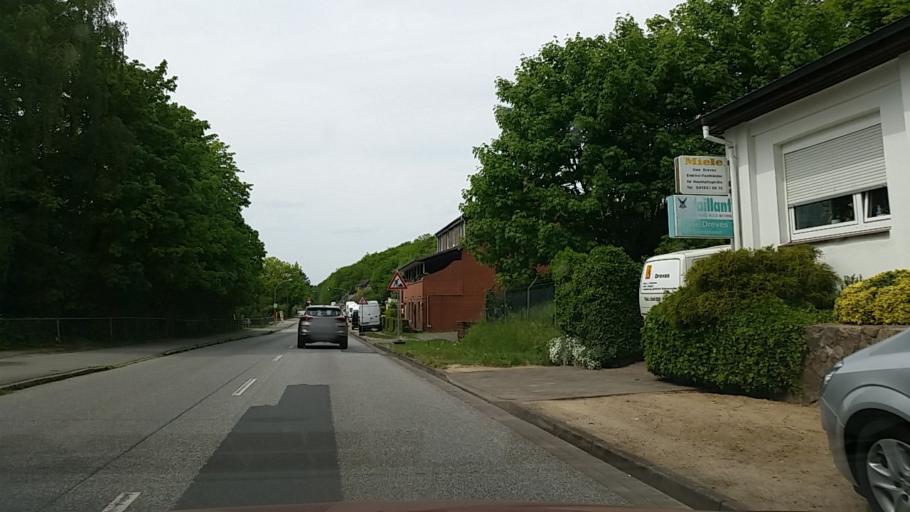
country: DE
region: Schleswig-Holstein
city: Escheburg
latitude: 53.4648
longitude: 10.3041
